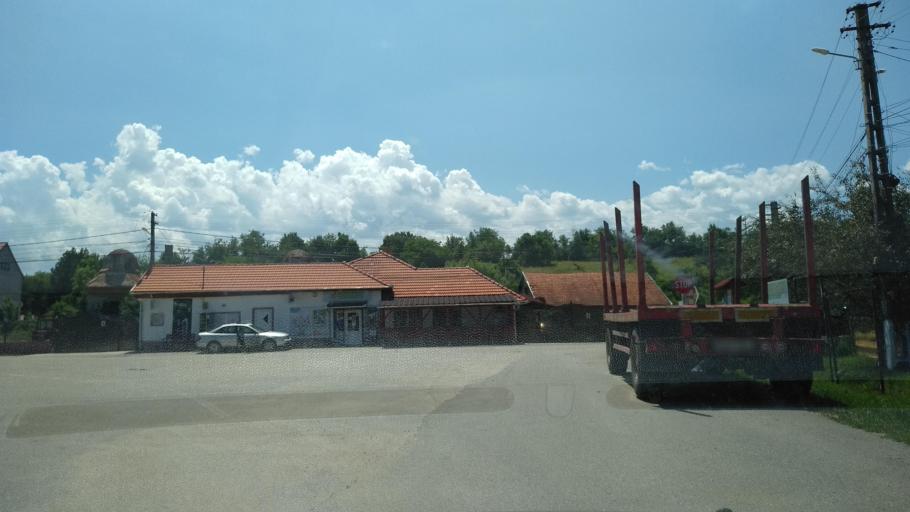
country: RO
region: Hunedoara
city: Densus
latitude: 45.5790
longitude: 22.8044
